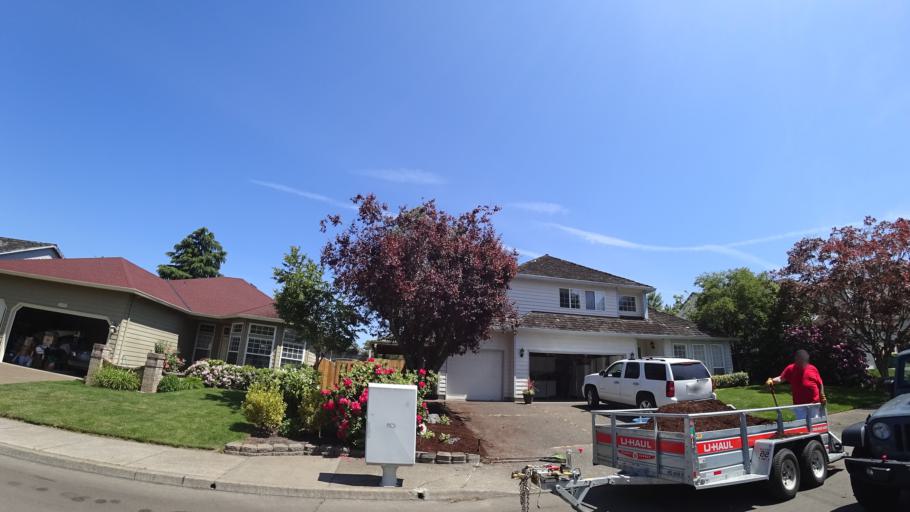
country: US
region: Oregon
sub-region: Washington County
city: King City
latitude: 45.4295
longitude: -122.8142
